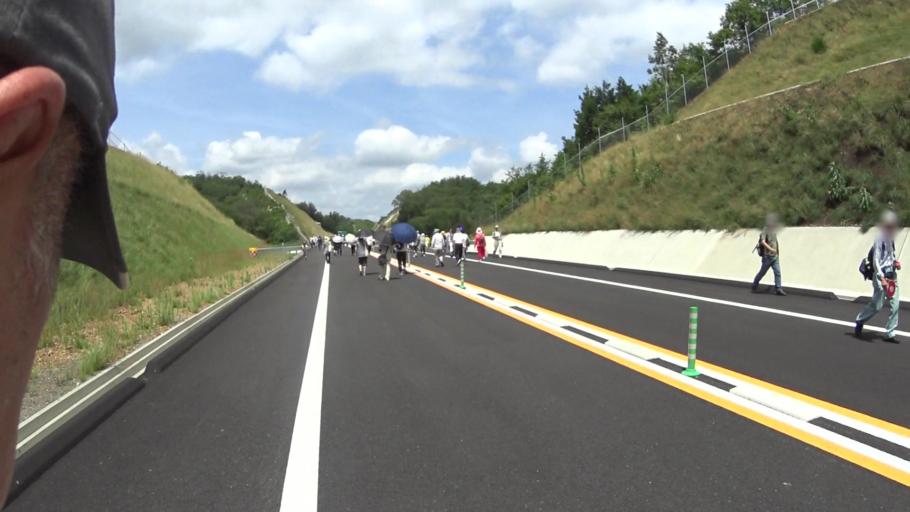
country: JP
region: Kyoto
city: Ayabe
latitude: 35.1675
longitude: 135.3796
